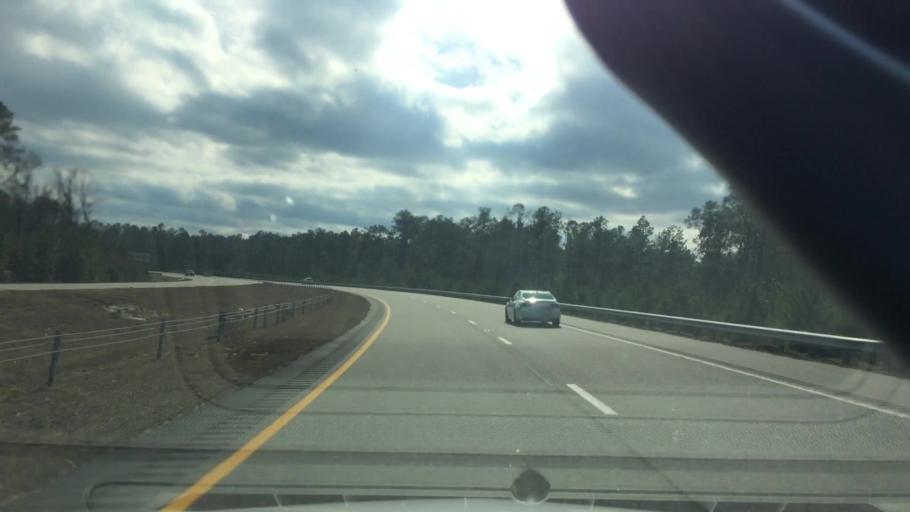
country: US
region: North Carolina
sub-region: Brunswick County
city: Leland
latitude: 34.2015
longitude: -78.0834
